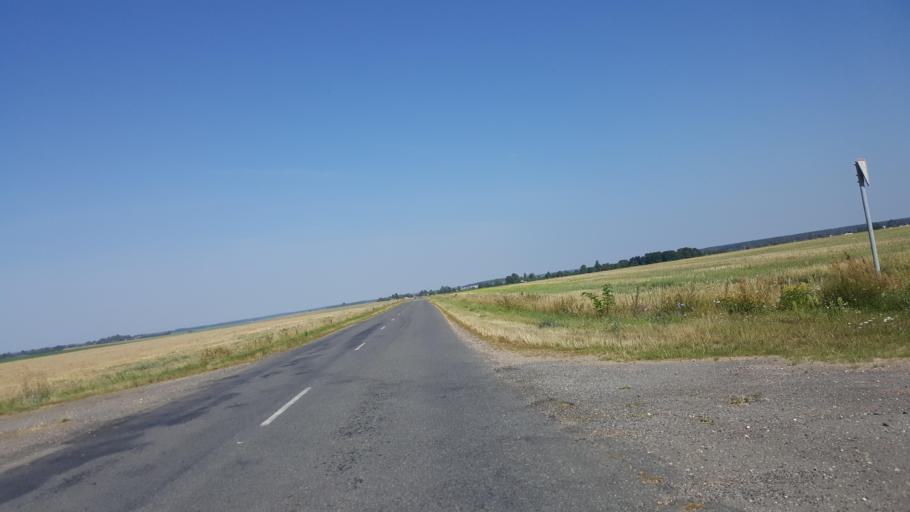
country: BY
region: Brest
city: Kamyanyets
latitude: 52.4532
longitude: 23.7281
